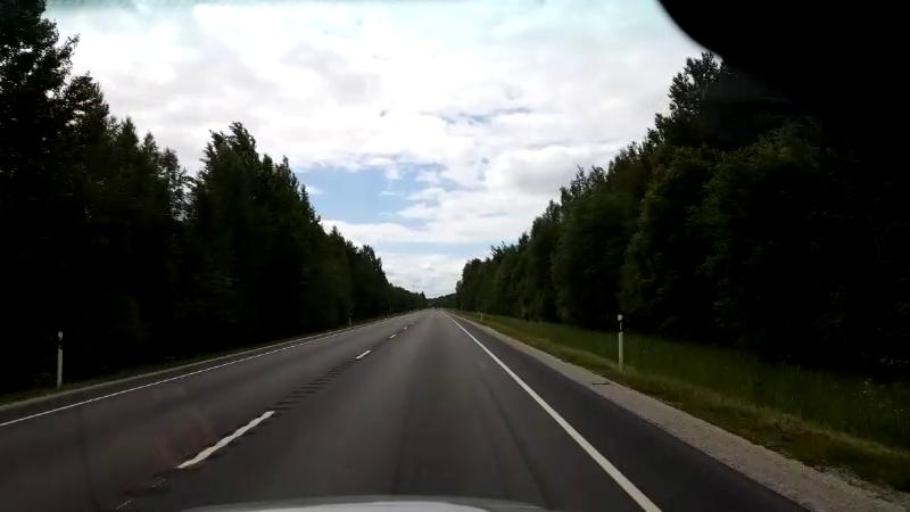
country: LV
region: Salacgrivas
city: Ainazi
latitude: 58.0977
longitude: 24.5080
